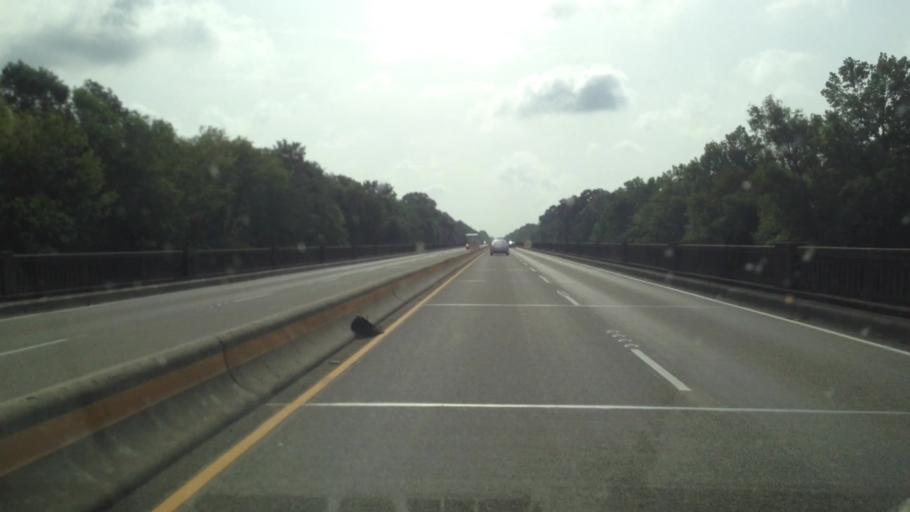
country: US
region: Louisiana
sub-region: Saint Landry Parish
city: Krotz Springs
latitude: 30.5550
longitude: -91.6828
